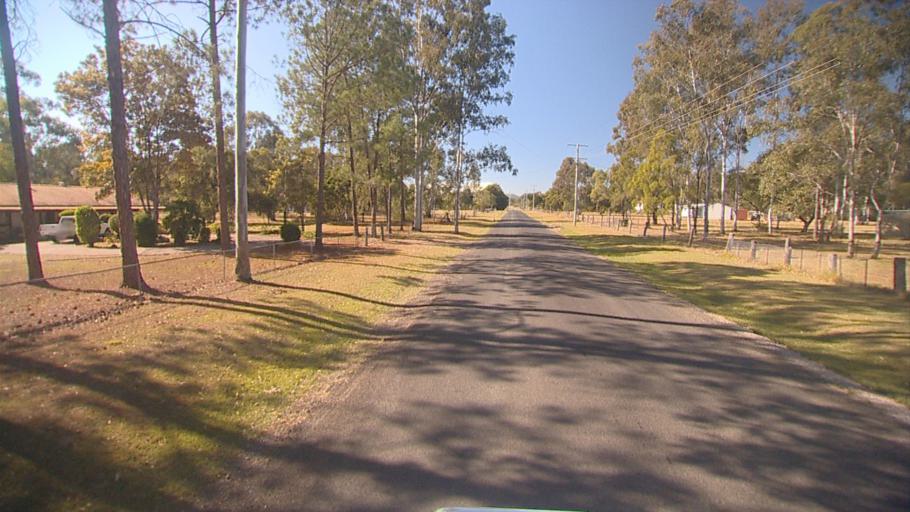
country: AU
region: Queensland
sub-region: Logan
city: Chambers Flat
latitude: -27.7569
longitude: 153.0731
